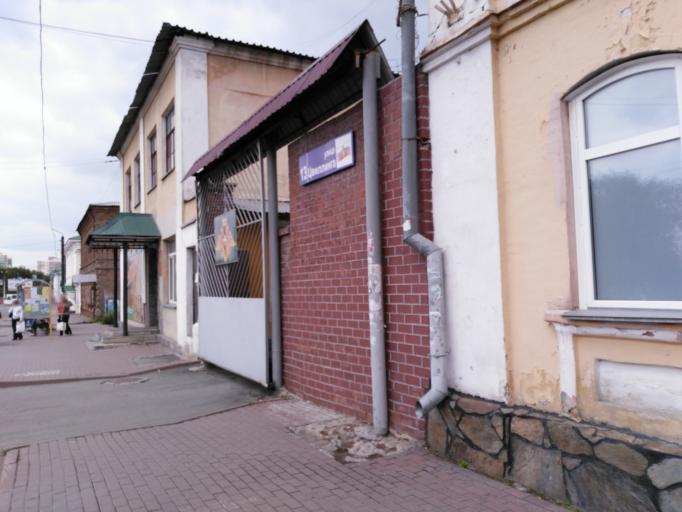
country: RU
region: Chelyabinsk
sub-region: Gorod Chelyabinsk
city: Chelyabinsk
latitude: 55.1664
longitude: 61.4037
